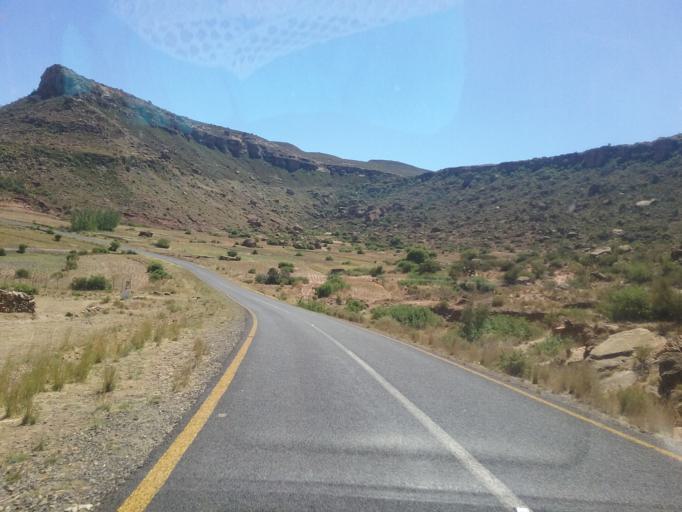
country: LS
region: Quthing
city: Quthing
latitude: -30.3108
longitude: 27.7397
